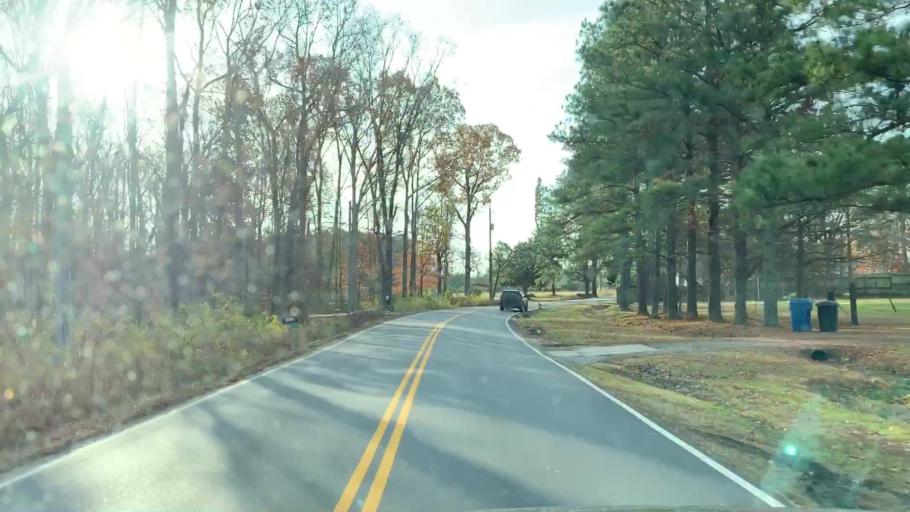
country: US
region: Virginia
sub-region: City of Virginia Beach
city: Virginia Beach
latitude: 36.7115
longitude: -76.0481
